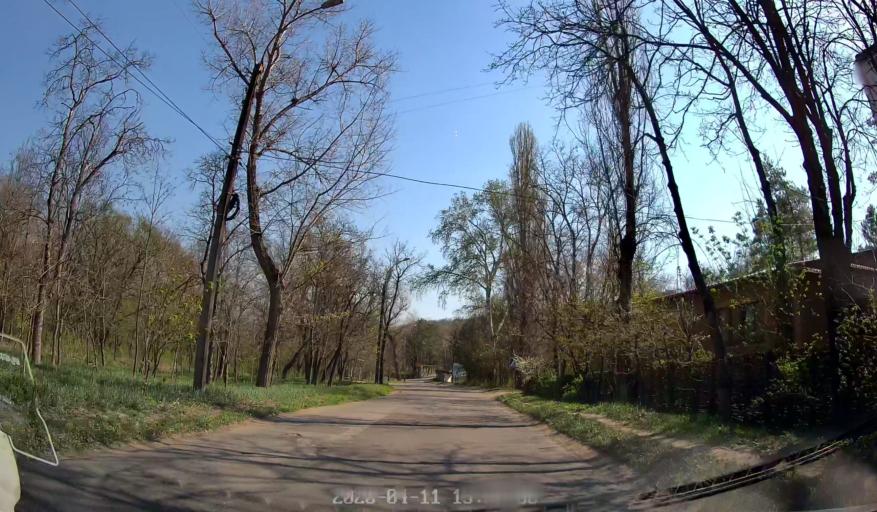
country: MD
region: Chisinau
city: Vadul lui Voda
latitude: 47.0802
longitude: 29.0927
